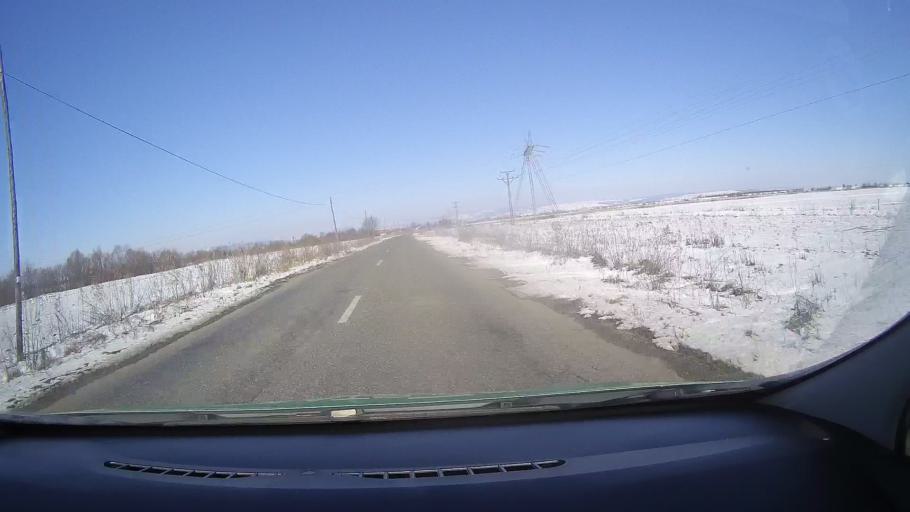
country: RO
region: Brasov
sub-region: Comuna Harseni
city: Harseni
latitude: 45.7740
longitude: 25.0013
